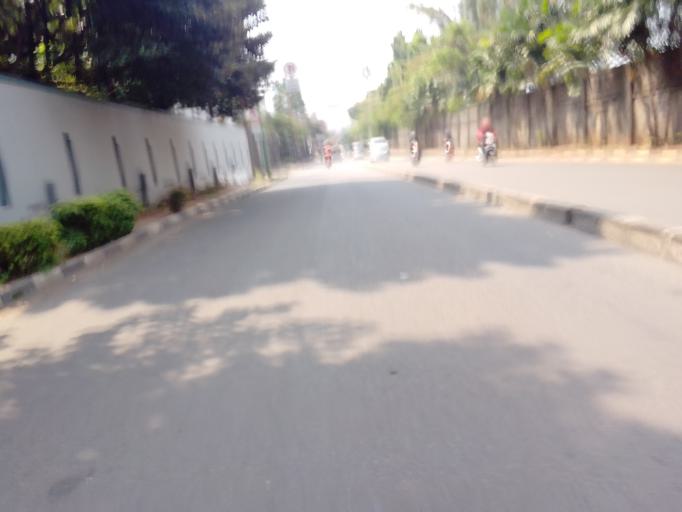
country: ID
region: Jakarta Raya
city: Jakarta
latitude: -6.2200
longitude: 106.7952
